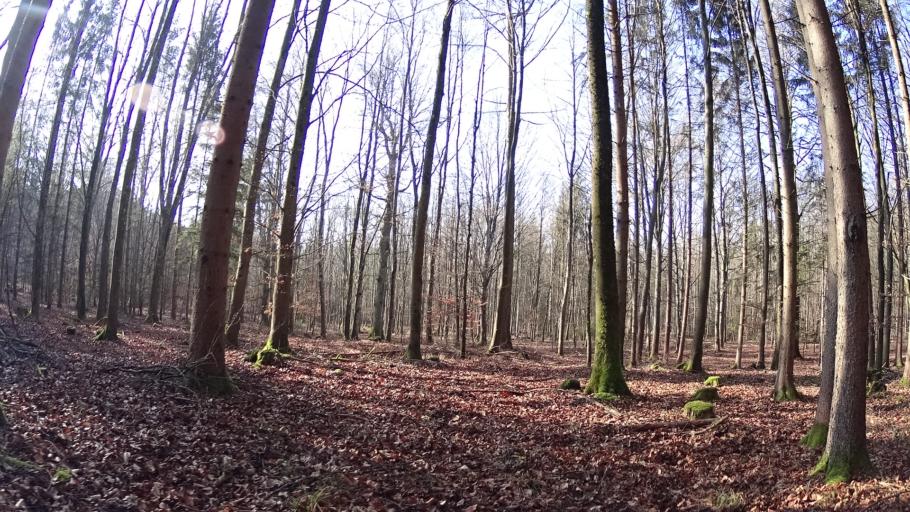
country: DE
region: Bavaria
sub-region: Upper Bavaria
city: Stammham
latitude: 48.8709
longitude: 11.4384
